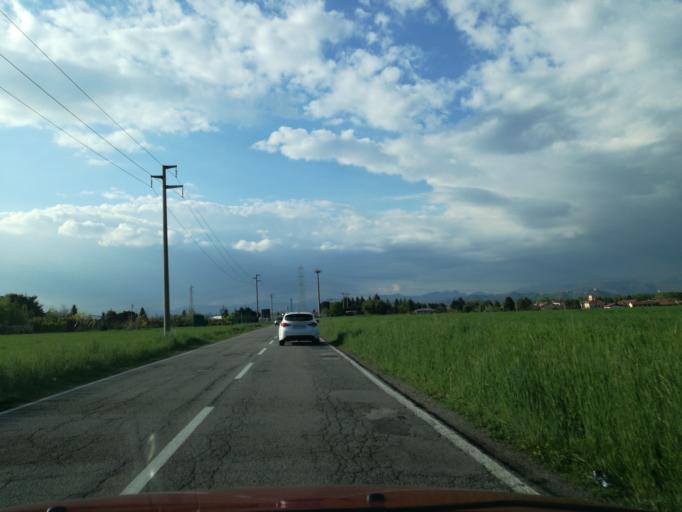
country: IT
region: Lombardy
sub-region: Provincia di Monza e Brianza
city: Velasca
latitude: 45.6340
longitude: 9.3669
